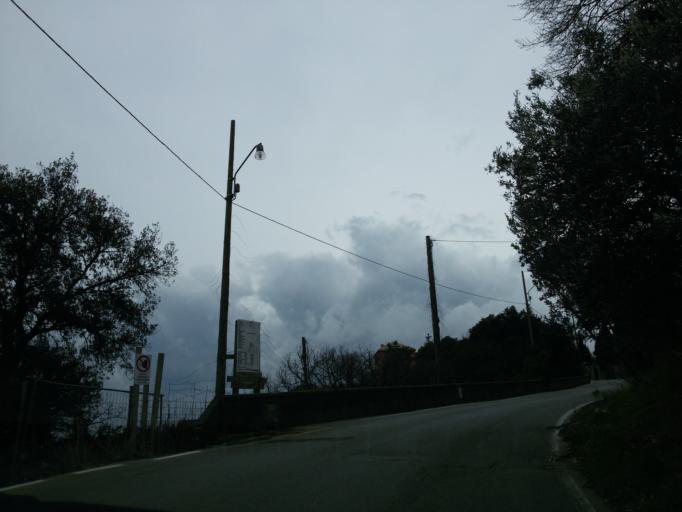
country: IT
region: Liguria
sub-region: Provincia di Genova
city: Genoa
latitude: 44.4159
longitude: 8.9763
